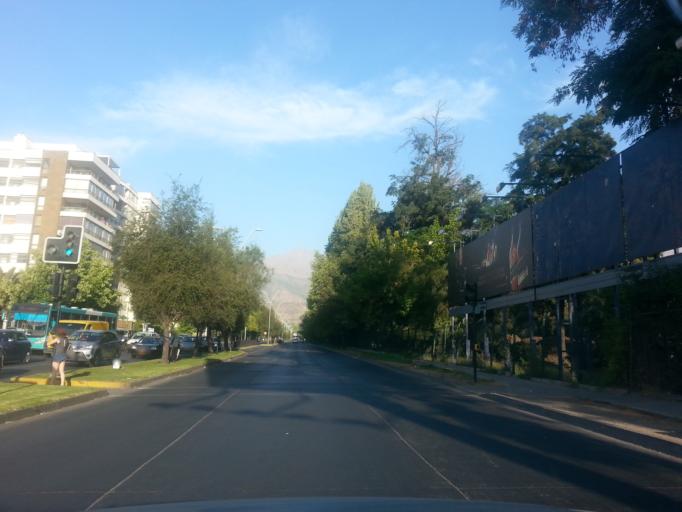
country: CL
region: Santiago Metropolitan
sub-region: Provincia de Santiago
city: Villa Presidente Frei, Nunoa, Santiago, Chile
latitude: -33.4311
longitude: -70.5651
